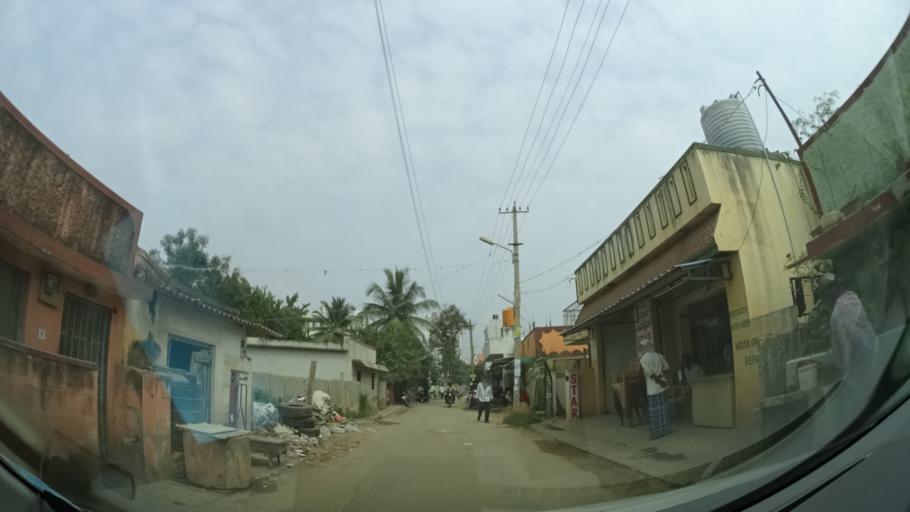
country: IN
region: Karnataka
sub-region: Bangalore Rural
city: Hoskote
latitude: 12.9705
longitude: 77.7530
